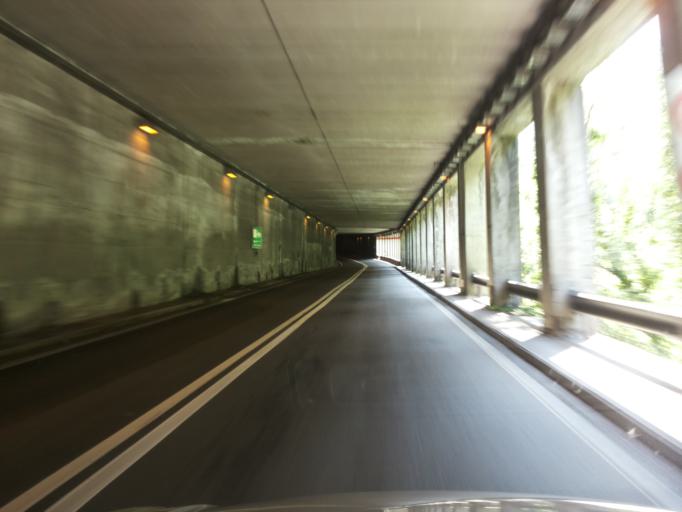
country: IT
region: Piedmont
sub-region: Provincia Verbano-Cusio-Ossola
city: Trontano
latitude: 46.1249
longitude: 8.3574
